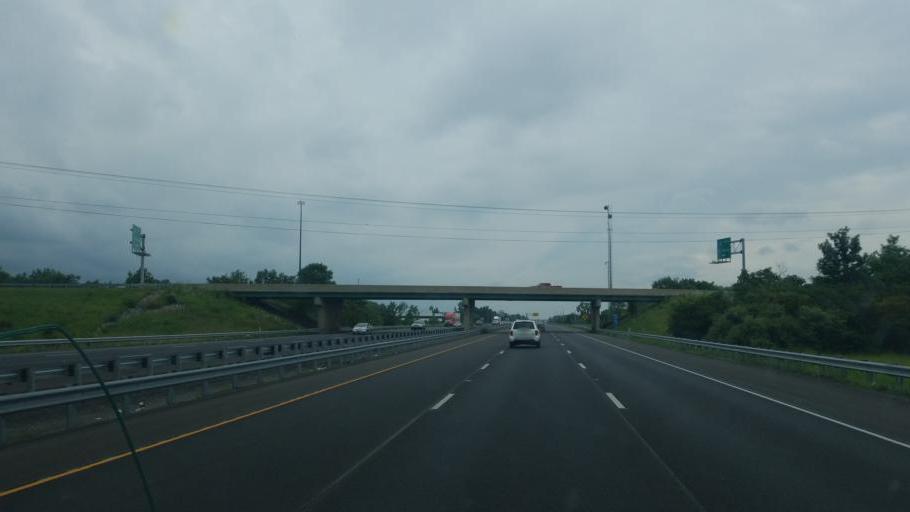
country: US
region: Indiana
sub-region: Madison County
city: Pendleton
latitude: 40.0039
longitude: -85.7726
